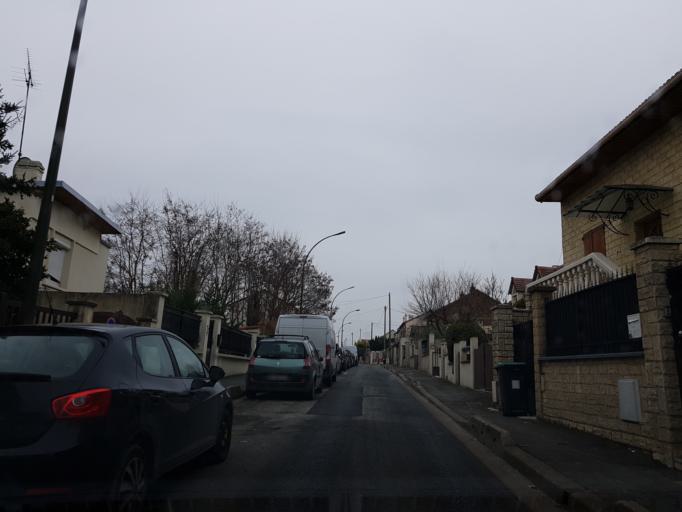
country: FR
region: Ile-de-France
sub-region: Departement du Val-de-Marne
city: Villejuif
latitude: 48.7999
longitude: 2.3693
